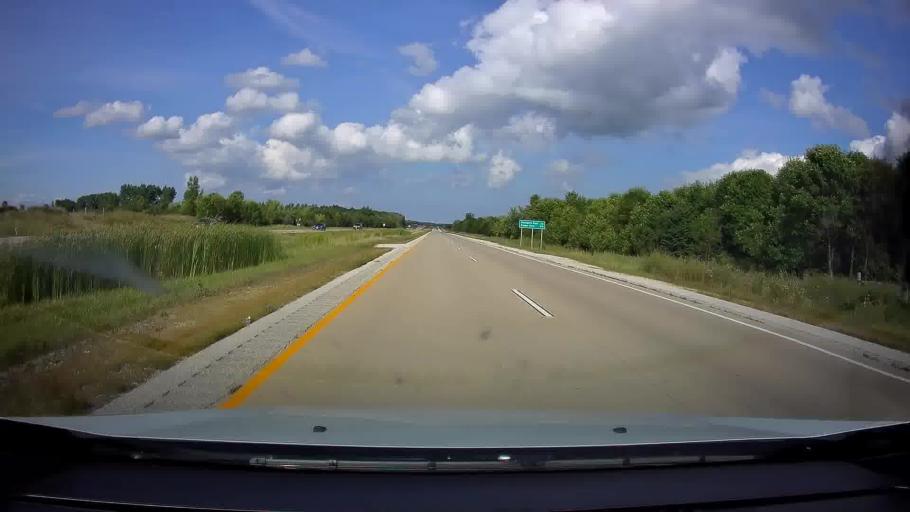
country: US
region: Wisconsin
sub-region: Kewaunee County
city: Luxemburg
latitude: 44.7222
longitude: -87.6111
